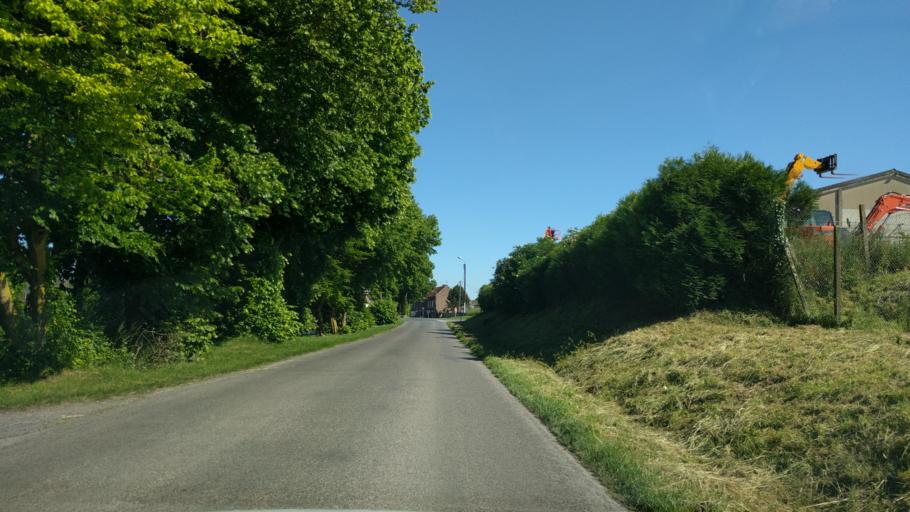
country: FR
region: Picardie
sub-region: Departement de la Somme
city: Peronne
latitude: 49.9174
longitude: 2.9311
